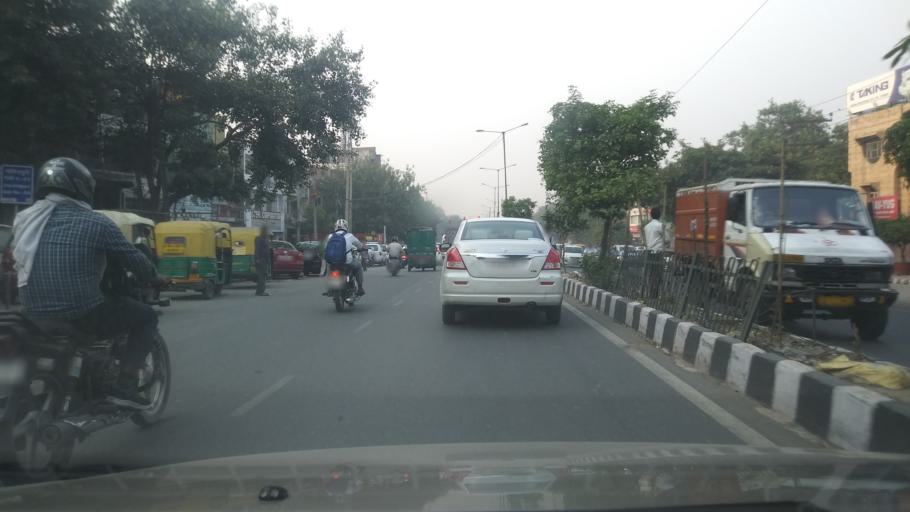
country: IN
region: Uttar Pradesh
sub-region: Gautam Buddha Nagar
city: Noida
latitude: 28.5353
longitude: 77.2679
